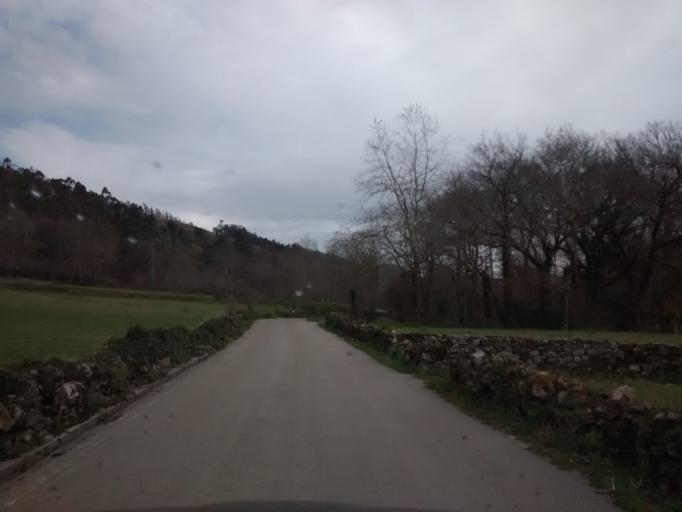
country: ES
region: Cantabria
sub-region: Provincia de Cantabria
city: Entrambasaguas
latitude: 43.3448
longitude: -3.6917
